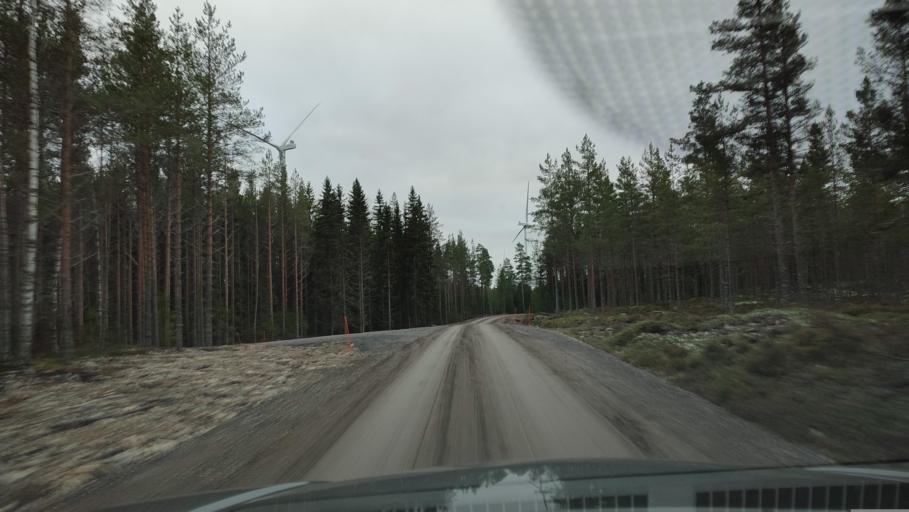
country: FI
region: Southern Ostrobothnia
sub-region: Suupohja
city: Karijoki
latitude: 62.1998
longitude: 21.5895
